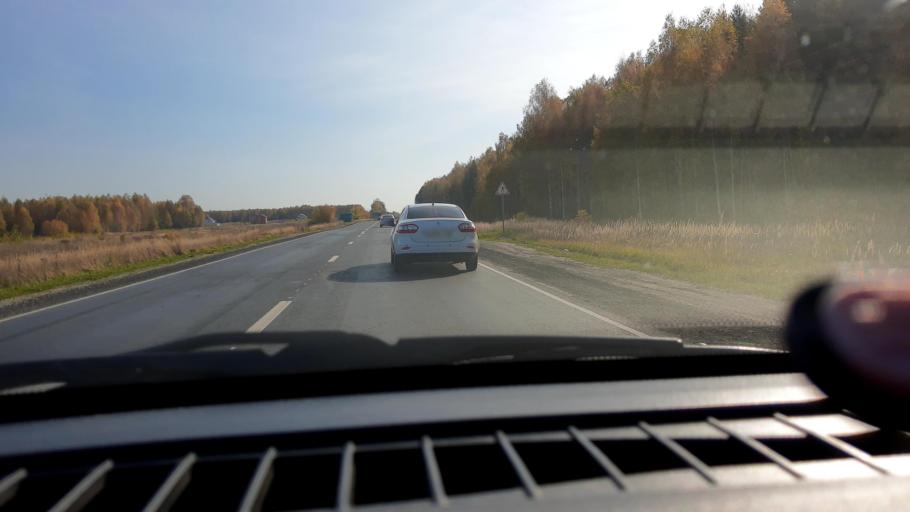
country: RU
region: Nizjnij Novgorod
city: Novaya Balakhna
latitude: 56.6102
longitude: 43.6053
